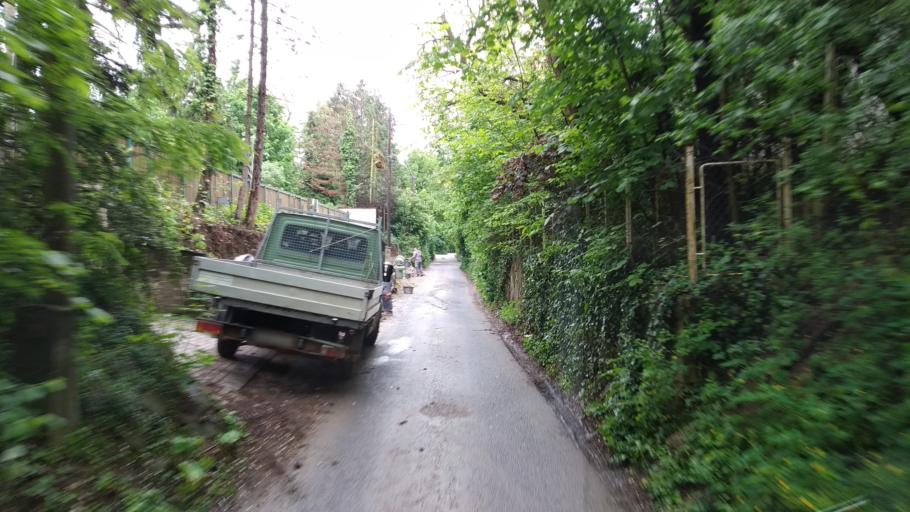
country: HU
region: Pest
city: Szentendre
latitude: 47.6903
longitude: 19.0813
